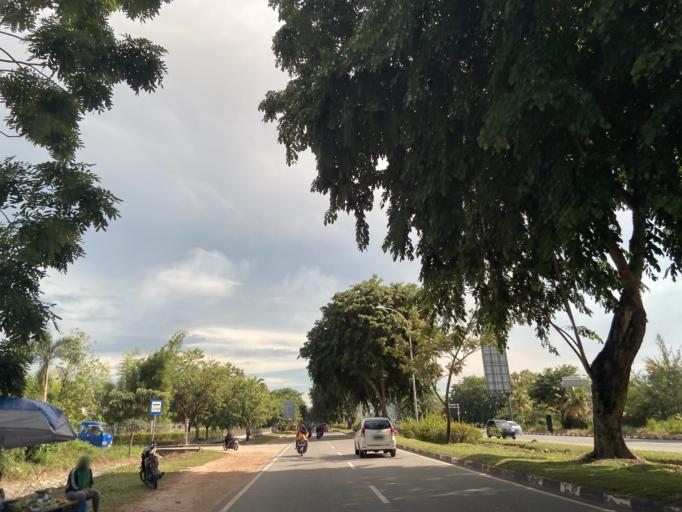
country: SG
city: Singapore
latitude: 1.1168
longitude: 104.0455
